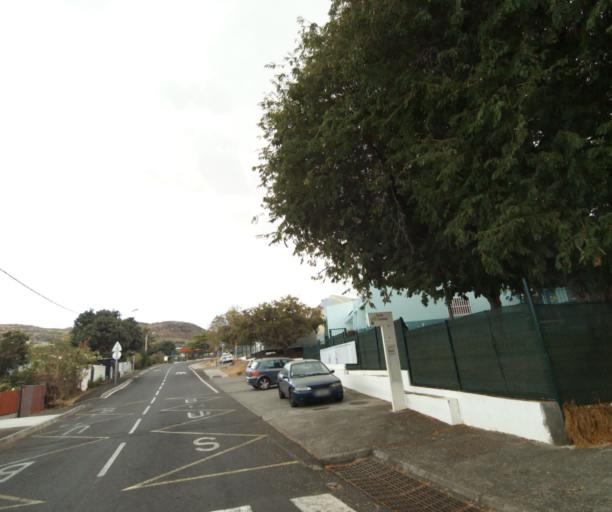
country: RE
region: Reunion
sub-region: Reunion
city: Saint-Paul
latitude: -21.0546
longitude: 55.2307
